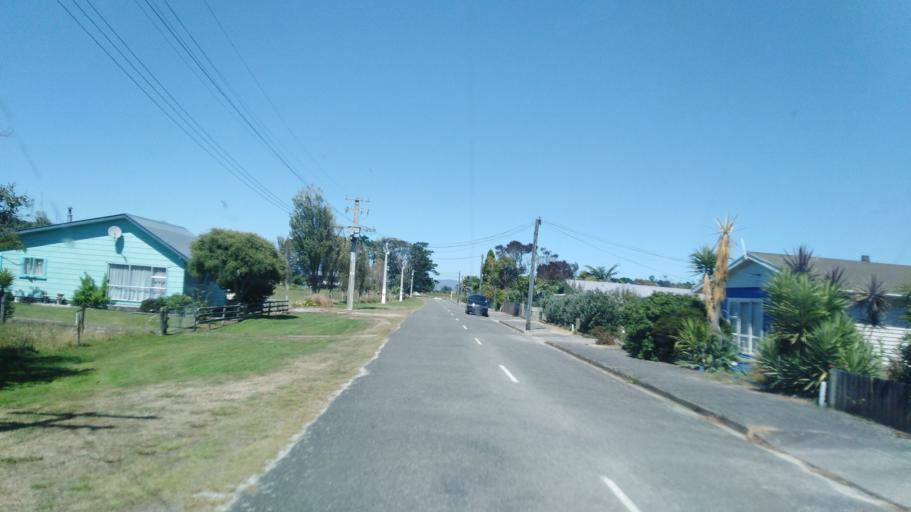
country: NZ
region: West Coast
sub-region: Buller District
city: Westport
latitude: -41.2493
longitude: 172.1109
